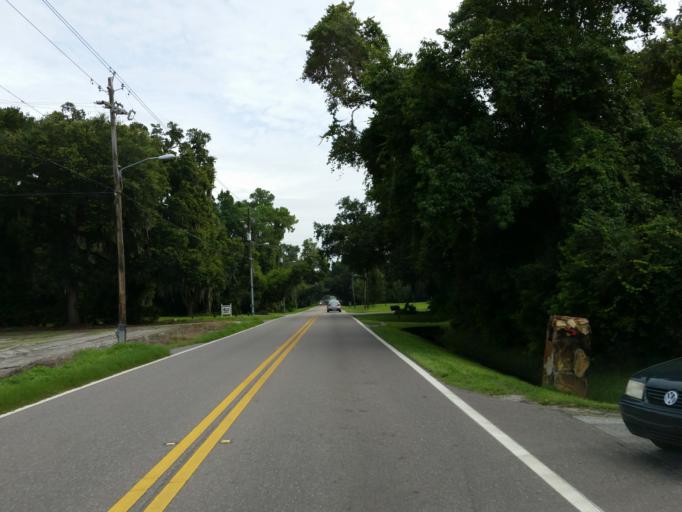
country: US
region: Florida
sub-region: Hillsborough County
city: Dover
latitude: 28.0062
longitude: -82.2445
